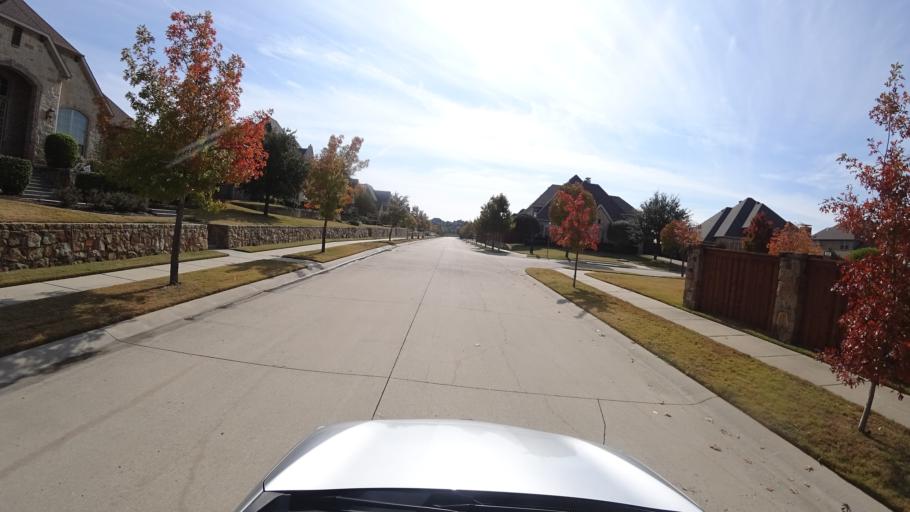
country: US
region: Texas
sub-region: Denton County
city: The Colony
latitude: 33.0417
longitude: -96.8878
